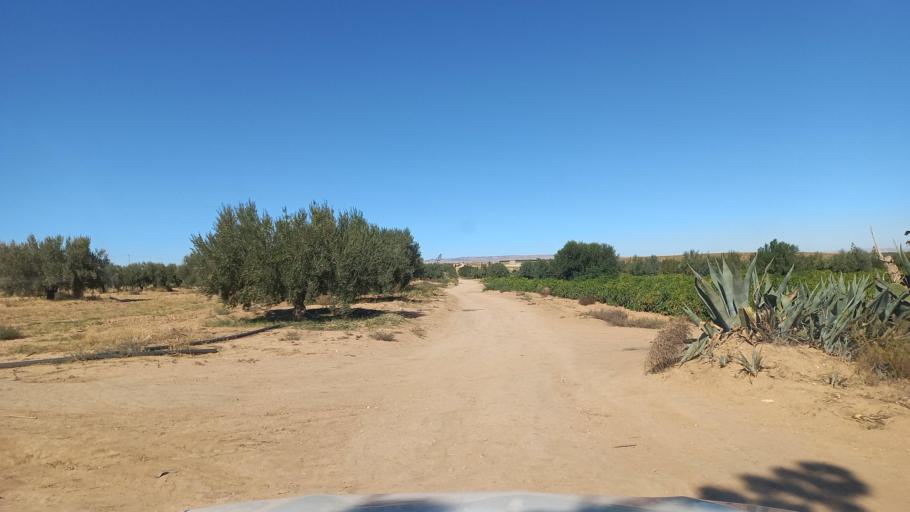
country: TN
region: Al Qasrayn
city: Sbiba
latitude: 35.4031
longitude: 9.0876
